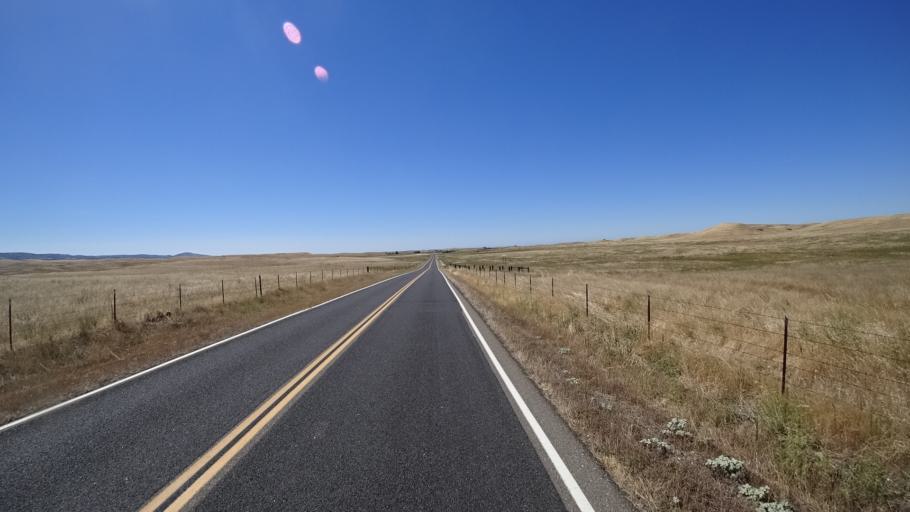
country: US
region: California
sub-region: Calaveras County
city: Rancho Calaveras
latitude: 38.0095
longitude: -120.8526
